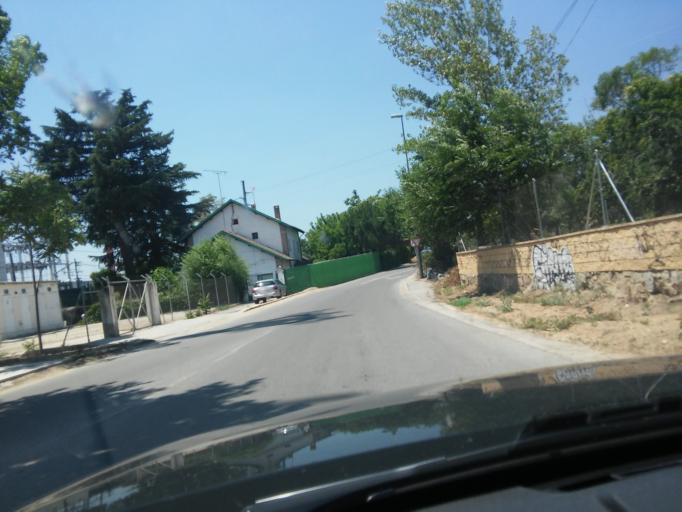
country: ES
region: Madrid
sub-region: Provincia de Madrid
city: Navalquejigo
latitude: 40.6098
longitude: -4.0461
